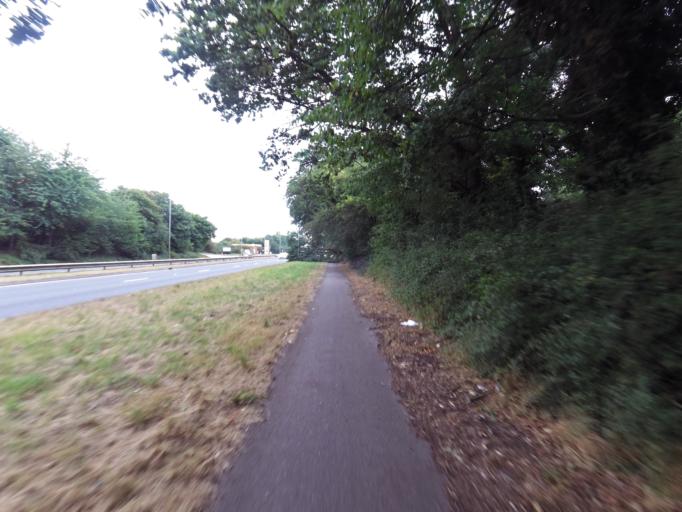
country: GB
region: England
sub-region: Hertfordshire
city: Shenley AV
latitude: 51.7392
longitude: -0.2772
